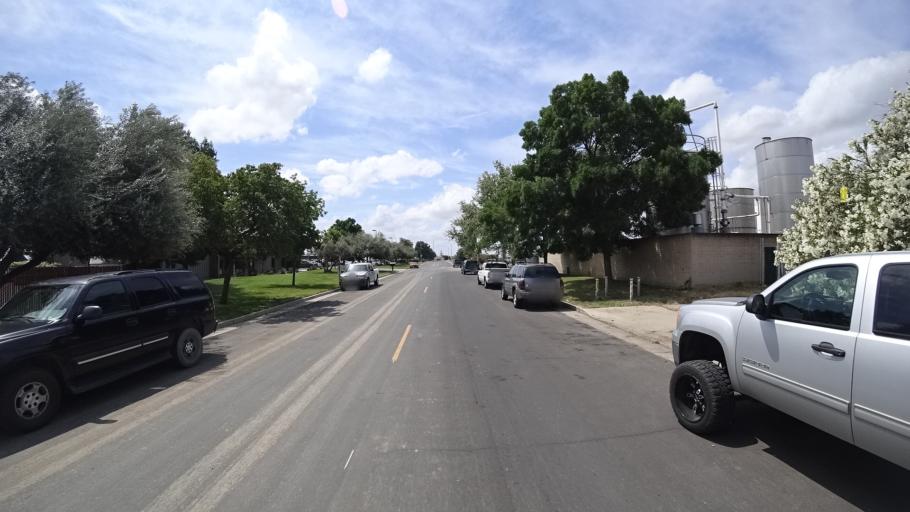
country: US
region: California
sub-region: Kings County
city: Home Garden
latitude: 36.2818
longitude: -119.6505
